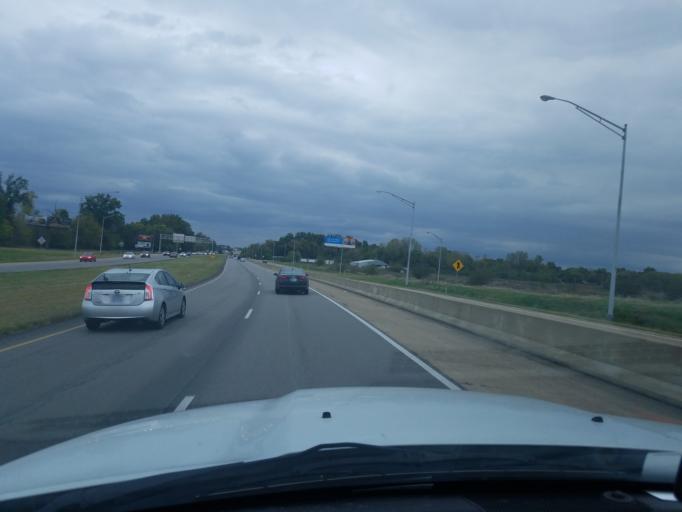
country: US
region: Indiana
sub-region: Vanderburgh County
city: Evansville
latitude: 37.9415
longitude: -87.5432
